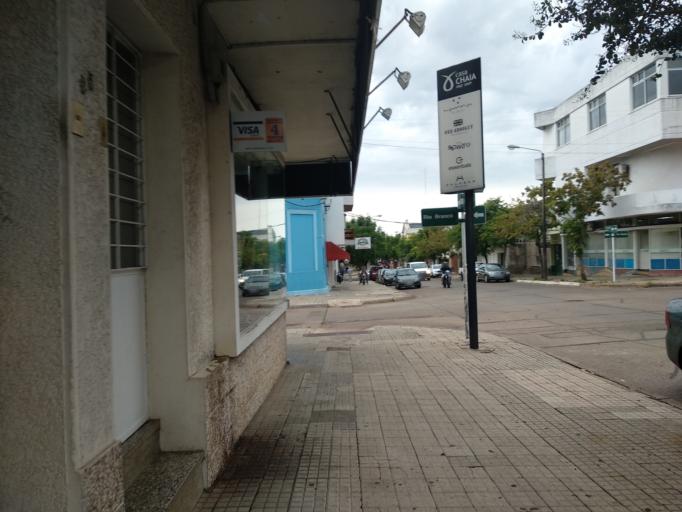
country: UY
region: Artigas
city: Artigas
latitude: -30.4005
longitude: -56.4668
